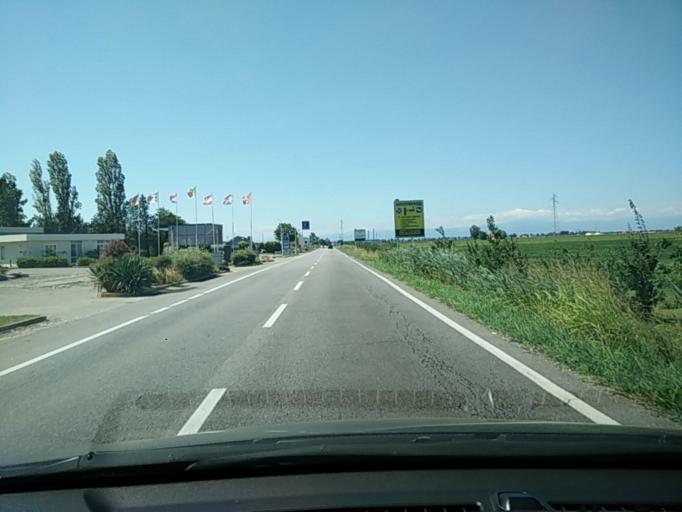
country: IT
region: Veneto
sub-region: Provincia di Venezia
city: La Salute di Livenza
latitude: 45.6525
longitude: 12.8342
